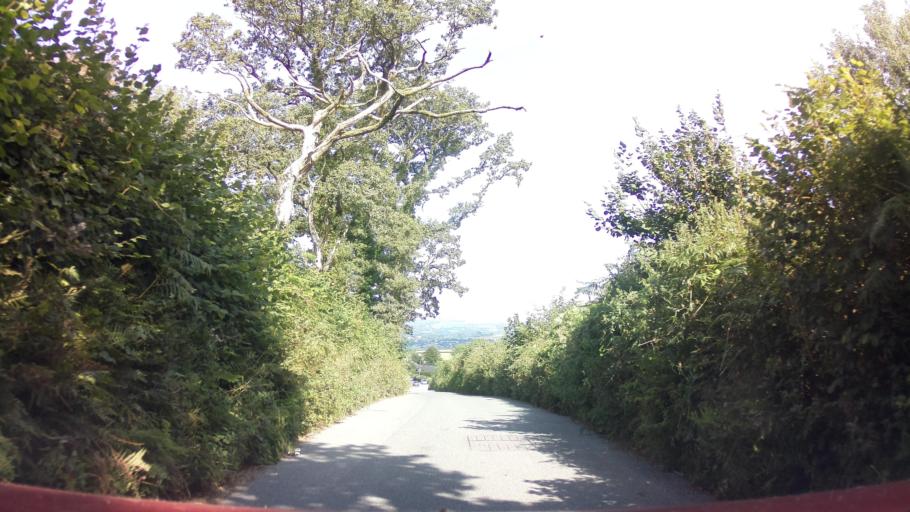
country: GB
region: England
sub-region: Cornwall
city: Gunnislake
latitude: 50.5322
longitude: -4.1879
